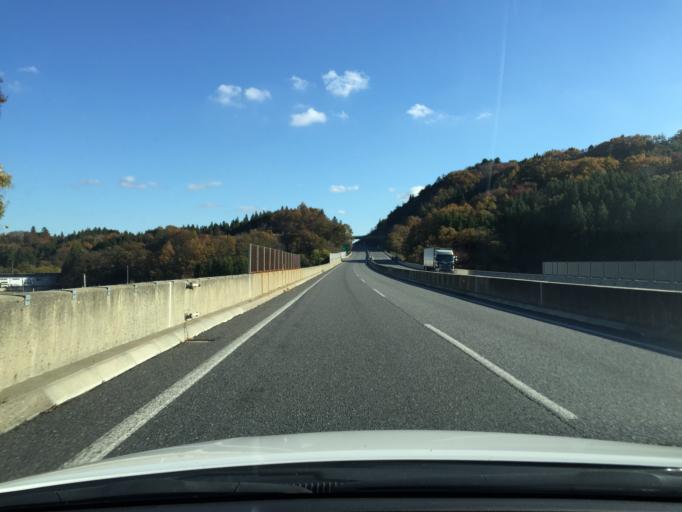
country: JP
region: Fukushima
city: Funehikimachi-funehiki
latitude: 37.2805
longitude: 140.6188
